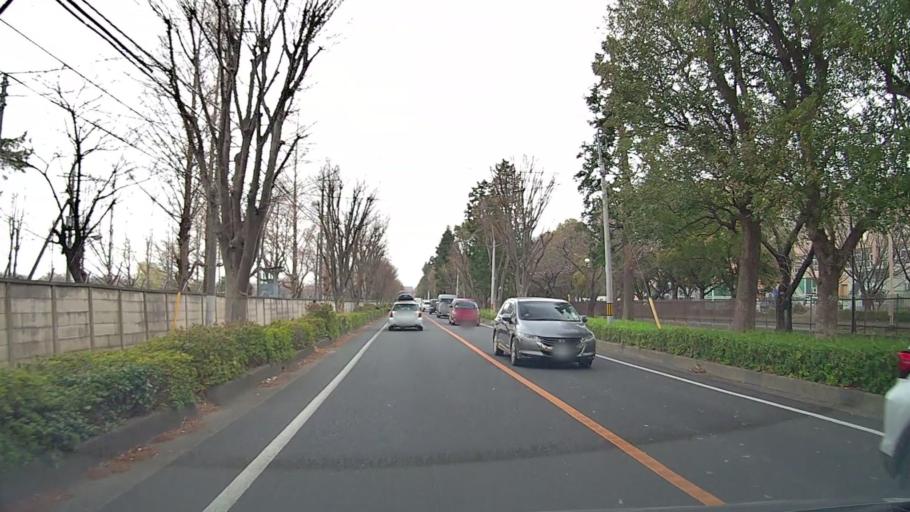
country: JP
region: Saitama
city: Asaka
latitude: 35.7832
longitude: 139.5906
